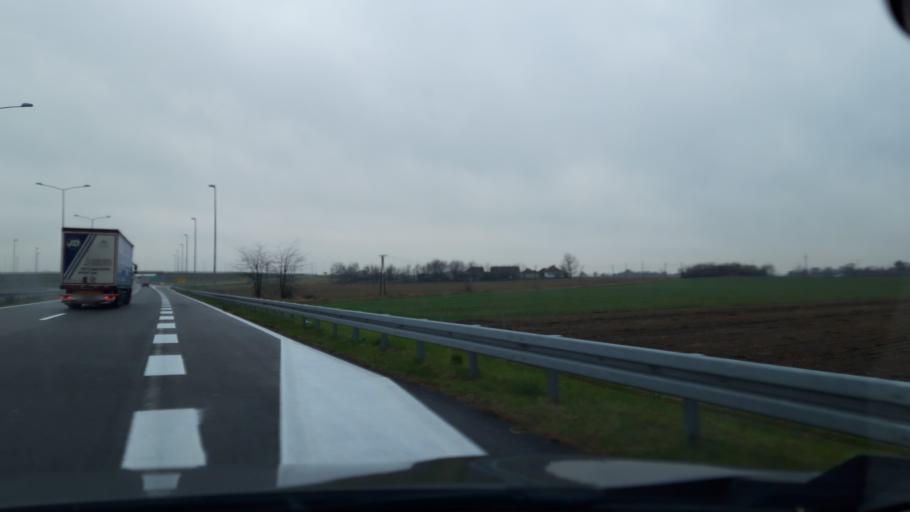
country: RS
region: Autonomna Pokrajina Vojvodina
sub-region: Severnobacki Okrug
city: Subotica
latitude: 46.0350
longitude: 19.7400
